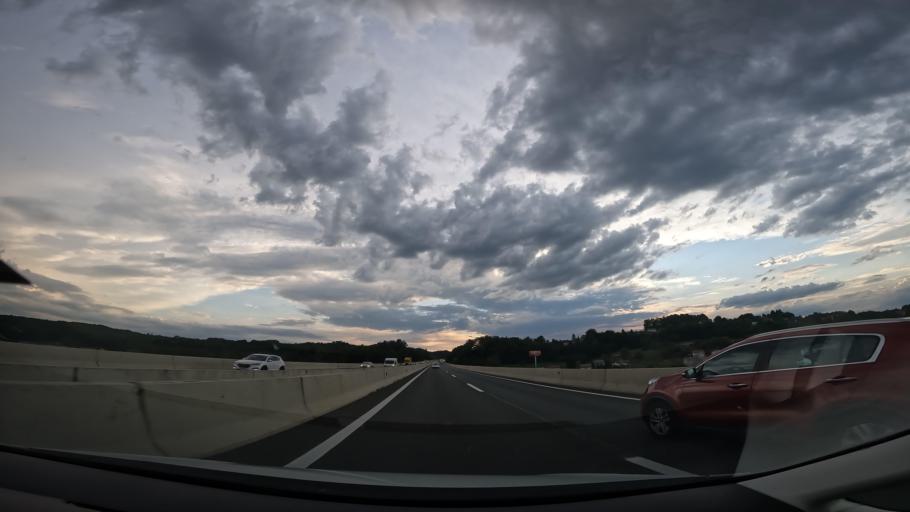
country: HR
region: Karlovacka
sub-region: Grad Karlovac
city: Karlovac
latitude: 45.5095
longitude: 15.5240
